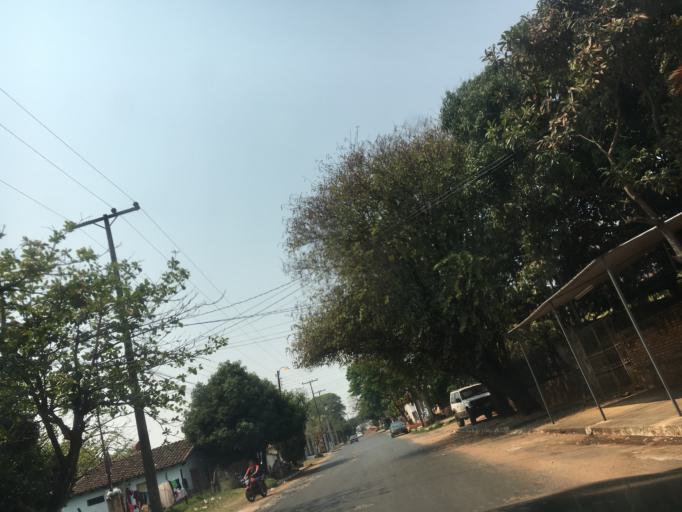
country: PY
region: Central
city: Villa Elisa
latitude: -25.3749
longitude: -57.5930
